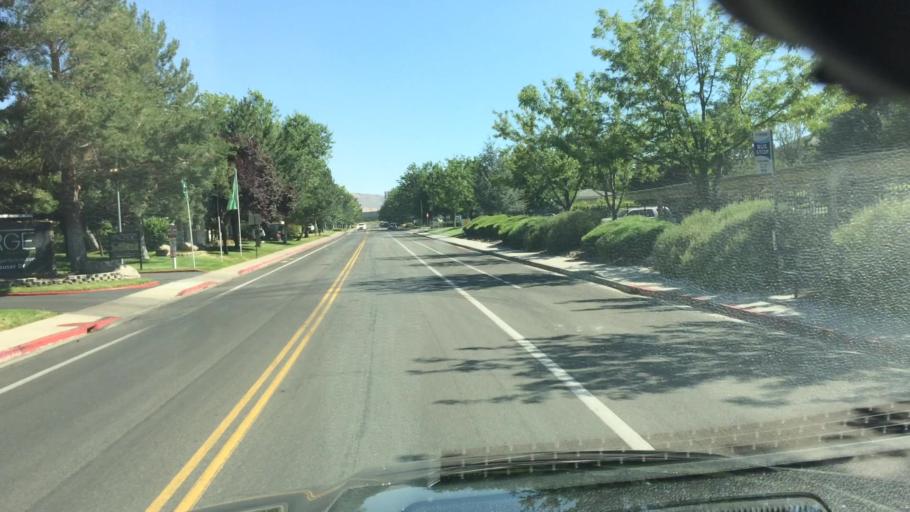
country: US
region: Nevada
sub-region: Washoe County
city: Sparks
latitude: 39.4524
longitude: -119.7712
